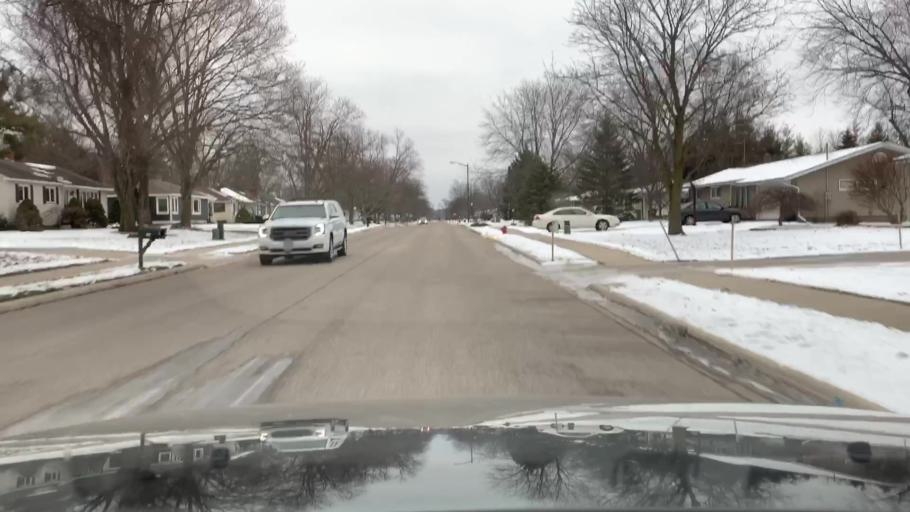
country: US
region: Michigan
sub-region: Ottawa County
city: Zeeland
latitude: 42.8063
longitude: -86.0342
